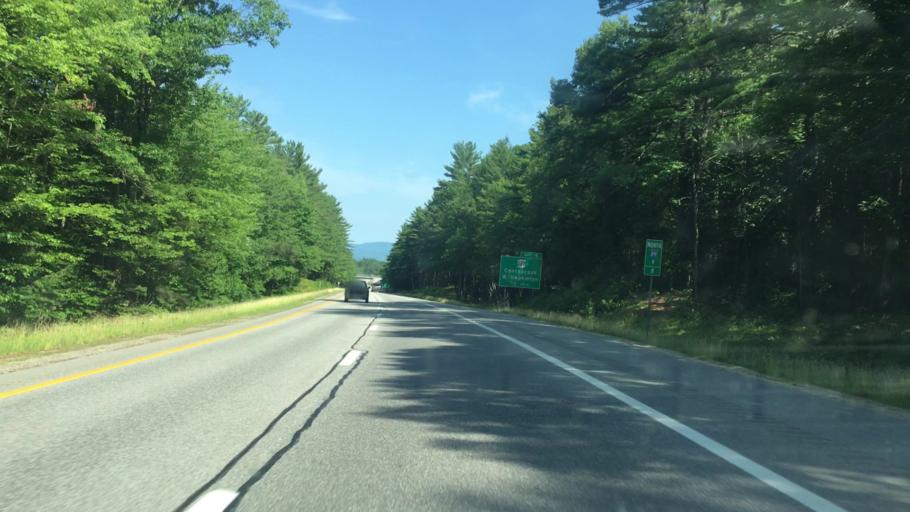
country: US
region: New Hampshire
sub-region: Merrimack County
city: Hopkinton
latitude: 43.1951
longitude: -71.7009
